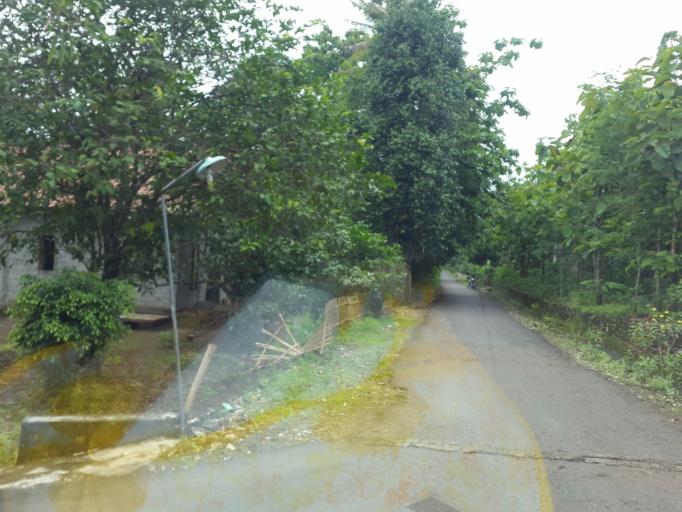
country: ID
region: Daerah Istimewa Yogyakarta
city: Wonosari
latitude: -7.9477
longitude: 110.6025
